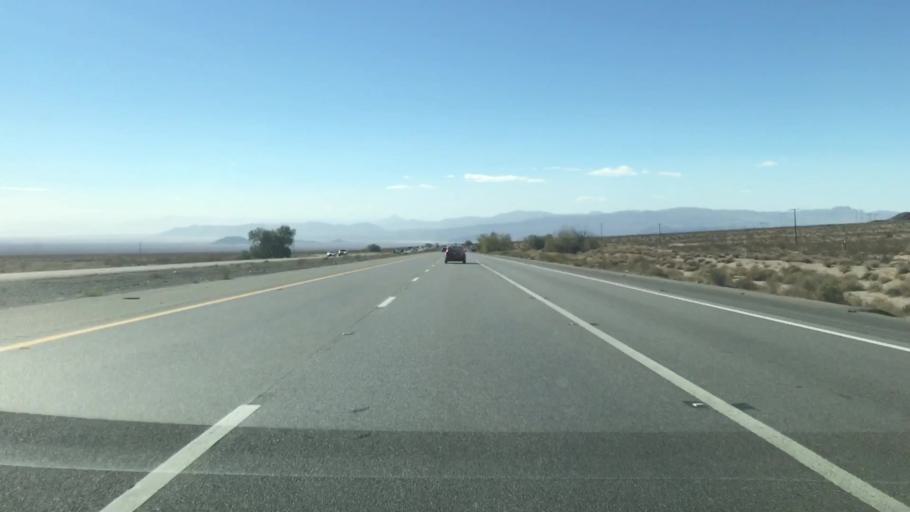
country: US
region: Nevada
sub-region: Clark County
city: Sandy Valley
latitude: 35.3614
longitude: -115.9234
